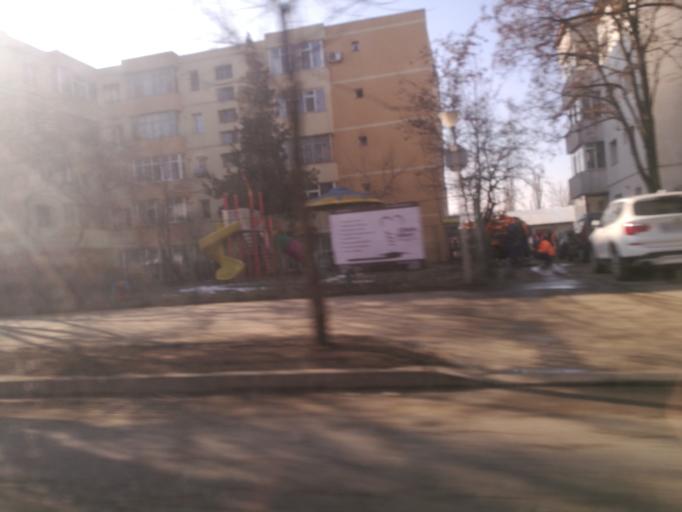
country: RO
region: Iasi
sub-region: Municipiul Iasi
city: Iasi
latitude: 47.1680
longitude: 27.5674
